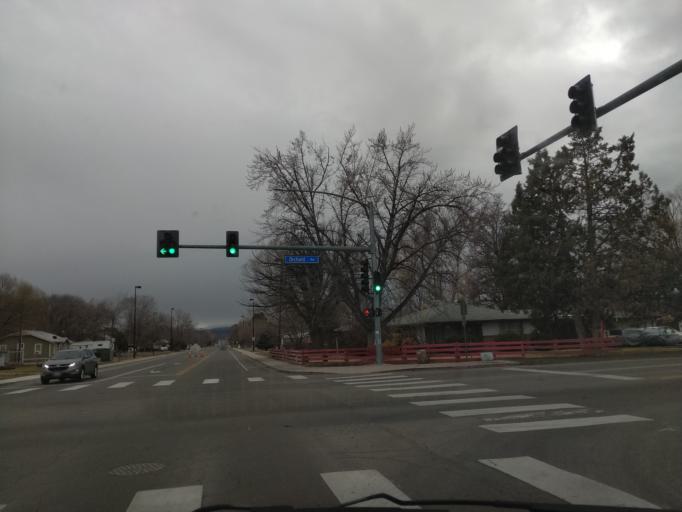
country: US
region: Colorado
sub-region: Mesa County
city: Fruitvale
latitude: 39.0848
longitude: -108.5152
